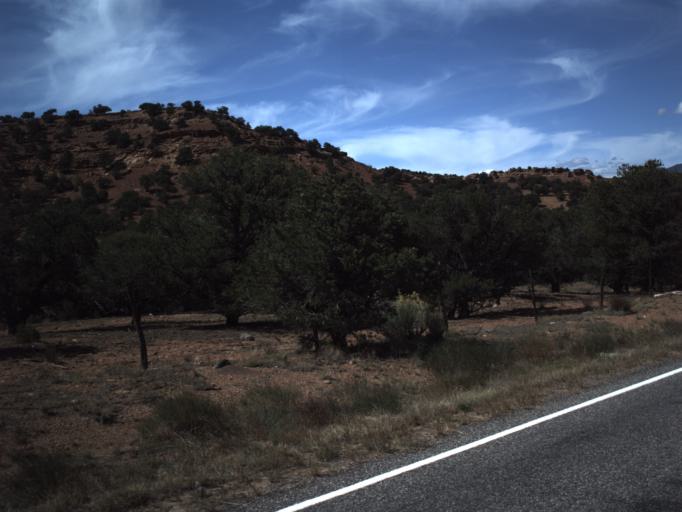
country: US
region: Utah
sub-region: Wayne County
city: Loa
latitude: 38.2511
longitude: -111.3784
